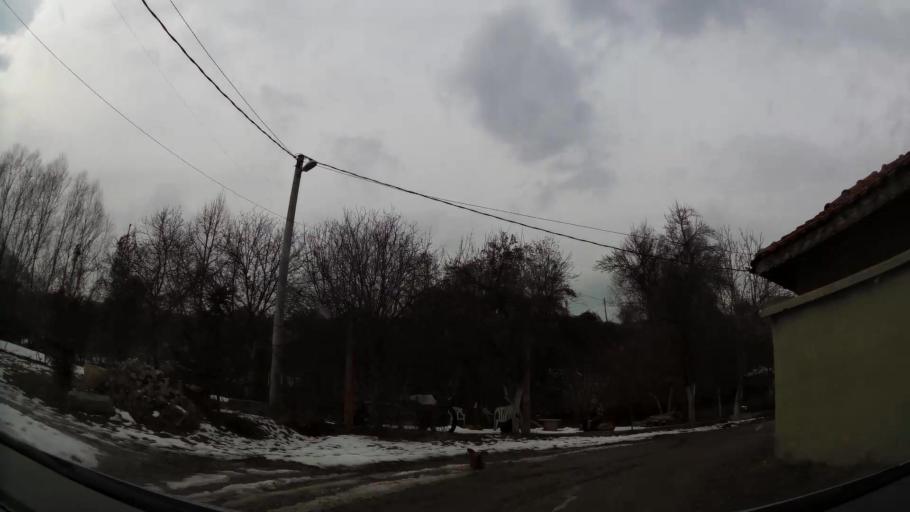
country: BG
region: Sofiya
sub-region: Obshtina Bozhurishte
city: Bozhurishte
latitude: 42.6950
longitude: 23.2181
